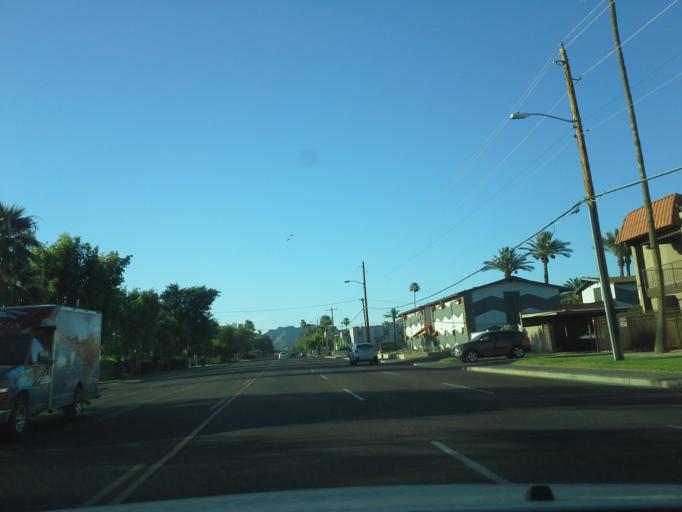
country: US
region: Arizona
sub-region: Maricopa County
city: Phoenix
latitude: 33.4827
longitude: -112.0129
